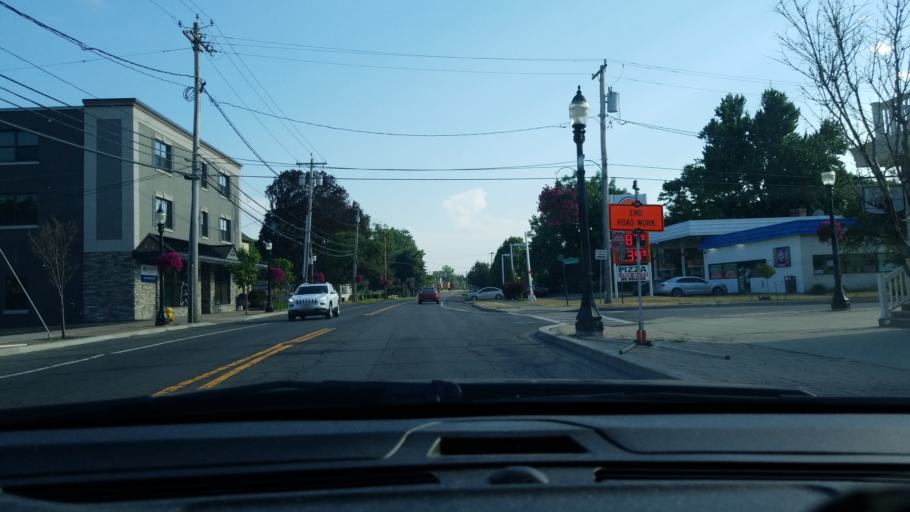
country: US
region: New York
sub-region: Onondaga County
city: North Syracuse
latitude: 43.1351
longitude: -76.1299
